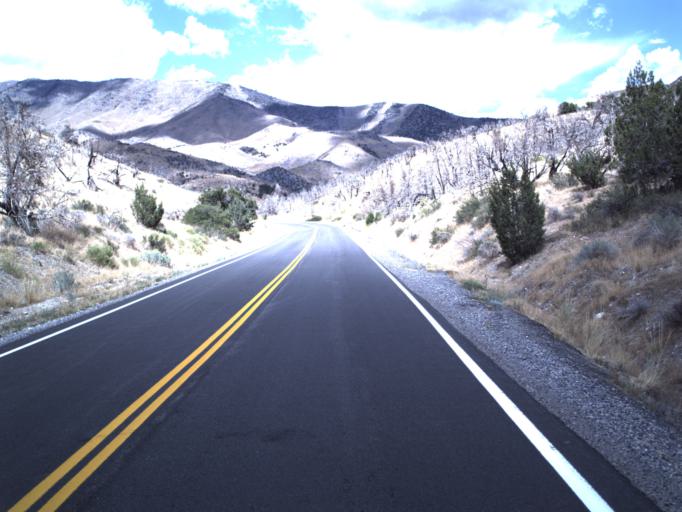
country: US
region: Utah
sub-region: Tooele County
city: Grantsville
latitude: 40.3305
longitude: -112.6192
